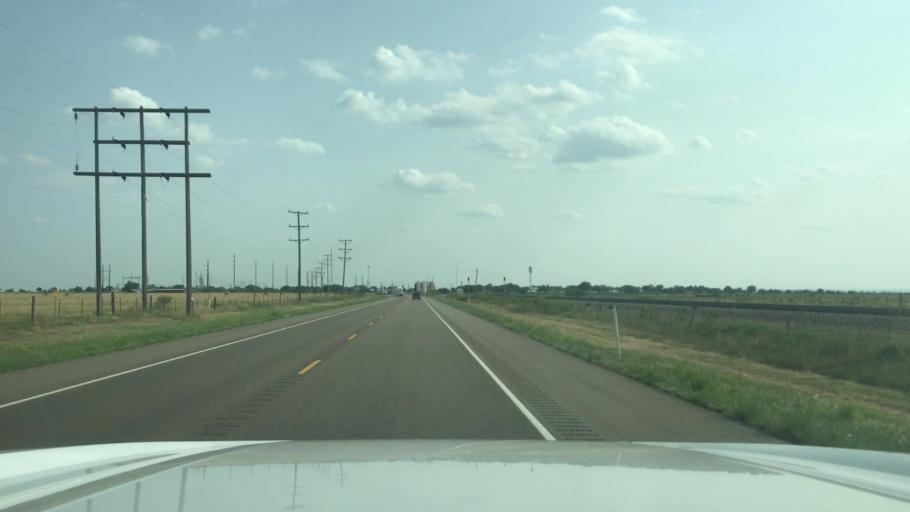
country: US
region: Texas
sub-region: Hartley County
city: Channing
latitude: 35.6981
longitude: -102.3273
